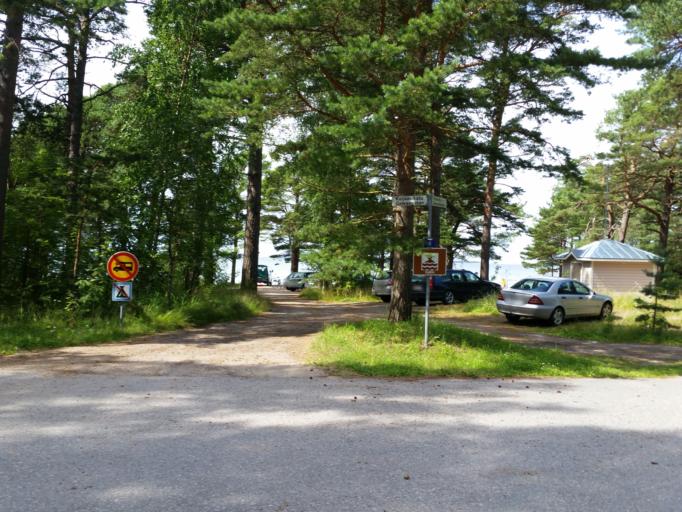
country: FI
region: Uusimaa
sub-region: Raaseporin
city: Hanko
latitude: 59.8314
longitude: 22.9276
